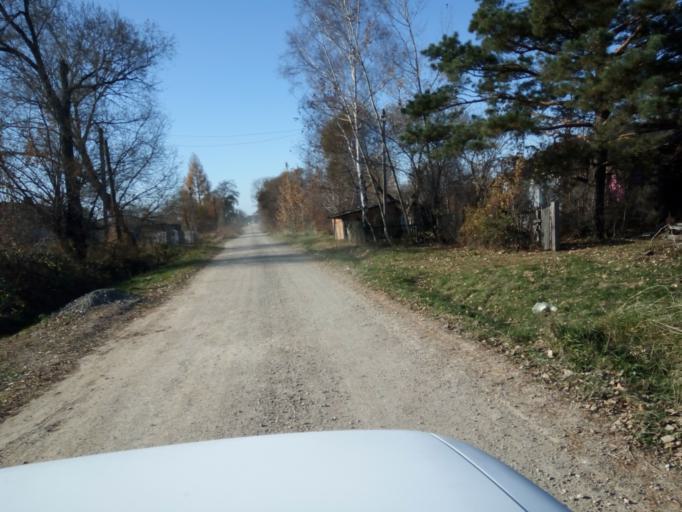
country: RU
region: Primorskiy
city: Lazo
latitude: 45.8759
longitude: 133.6567
